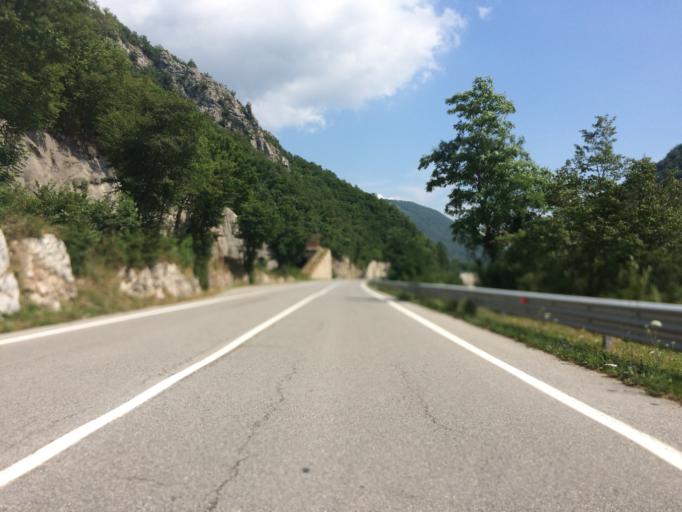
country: IT
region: Piedmont
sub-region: Provincia di Cuneo
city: Garessio
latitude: 44.1734
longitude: 7.9776
